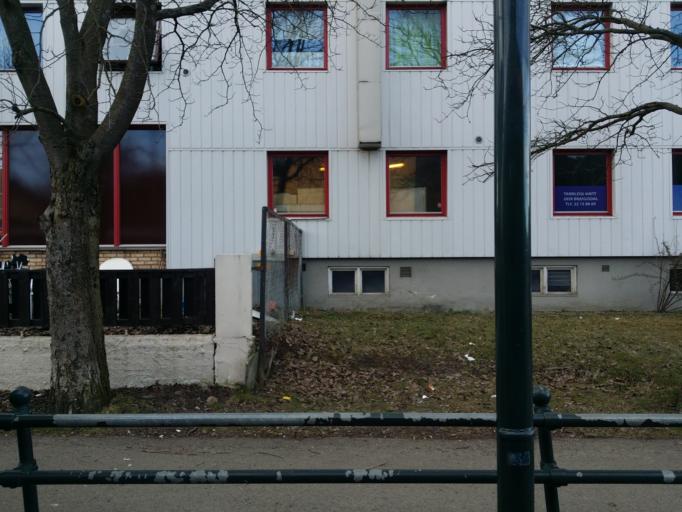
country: NO
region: Oslo
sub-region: Oslo
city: Oslo
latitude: 59.9560
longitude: 10.7855
